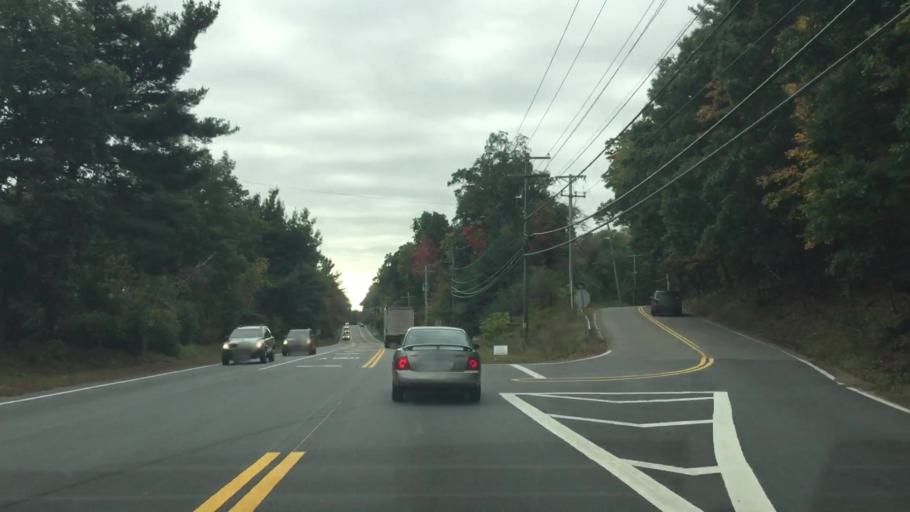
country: US
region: Massachusetts
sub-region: Essex County
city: Andover
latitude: 42.6461
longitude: -71.0891
